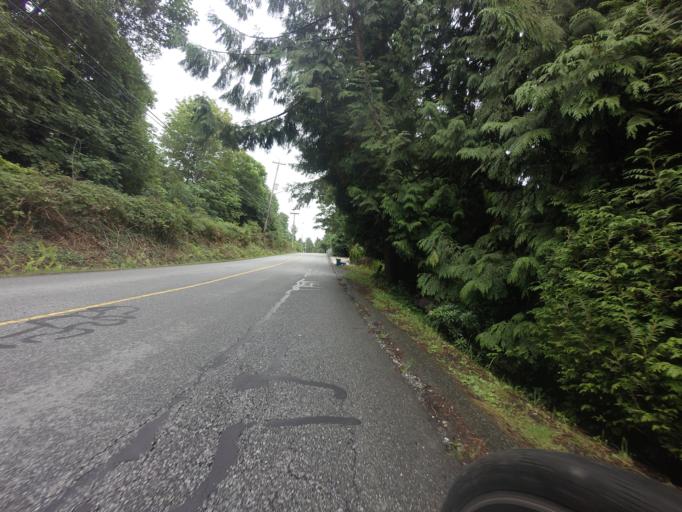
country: CA
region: British Columbia
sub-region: Greater Vancouver Regional District
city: Bowen Island
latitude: 49.3433
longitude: -123.2657
